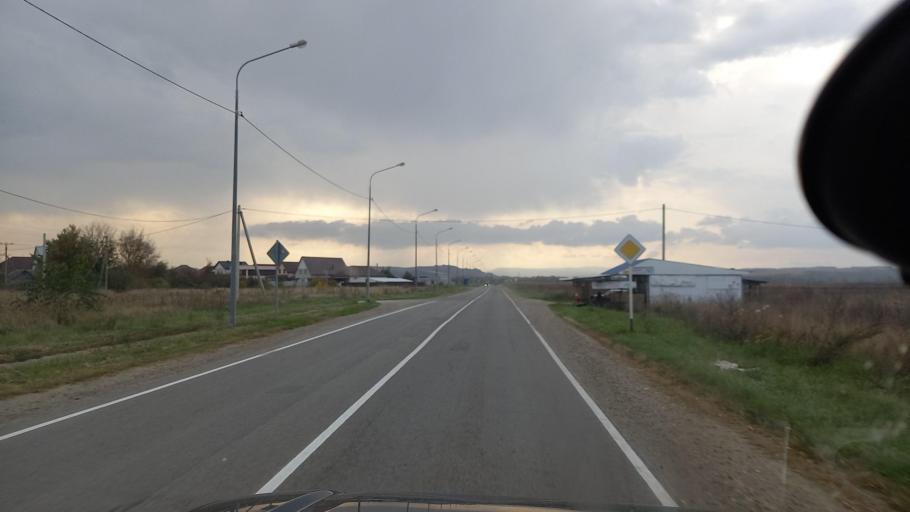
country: RU
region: Krasnodarskiy
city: Mostovskoy
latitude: 44.3957
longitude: 40.7708
